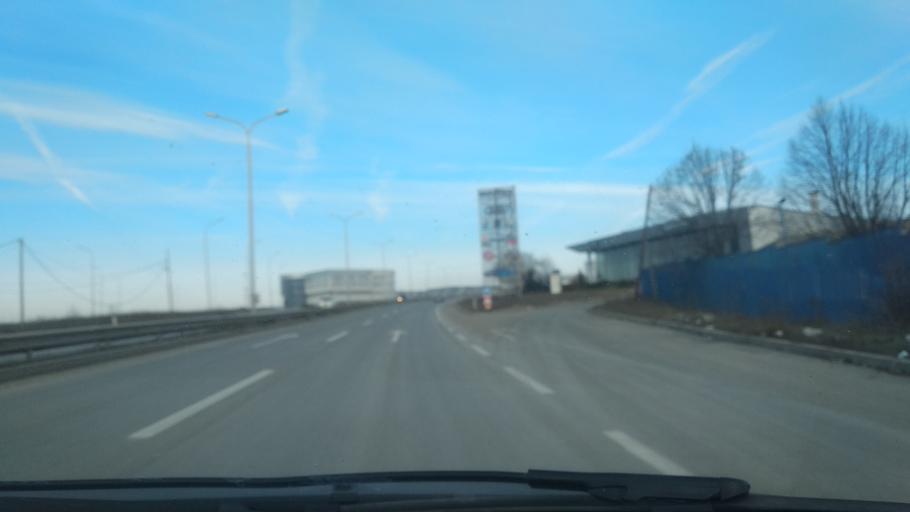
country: XK
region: Pristina
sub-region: Kosovo Polje
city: Kosovo Polje
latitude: 42.6709
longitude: 21.1177
